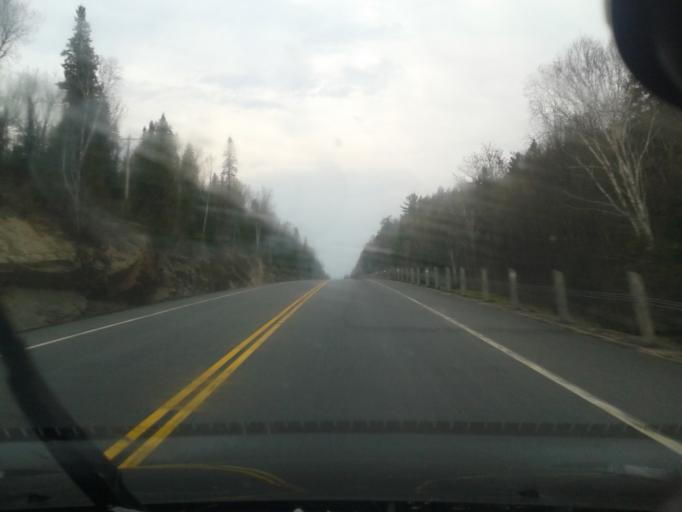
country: CA
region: Ontario
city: Huntsville
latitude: 45.4767
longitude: -78.7679
